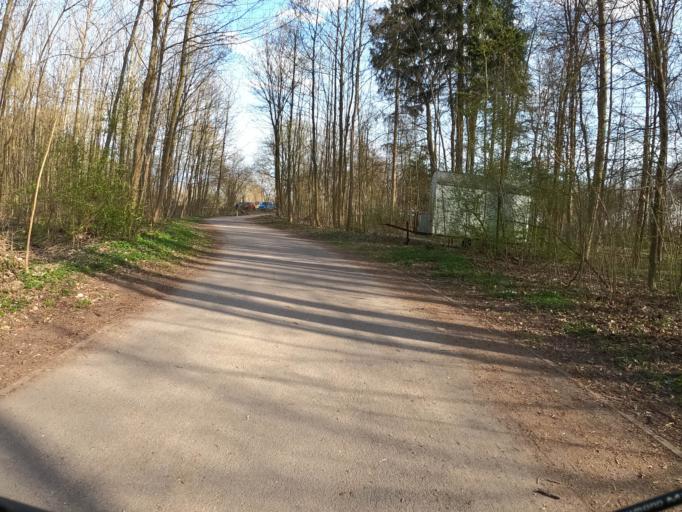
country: DE
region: Bavaria
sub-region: Swabia
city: Neu-Ulm
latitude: 48.4266
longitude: 10.0439
